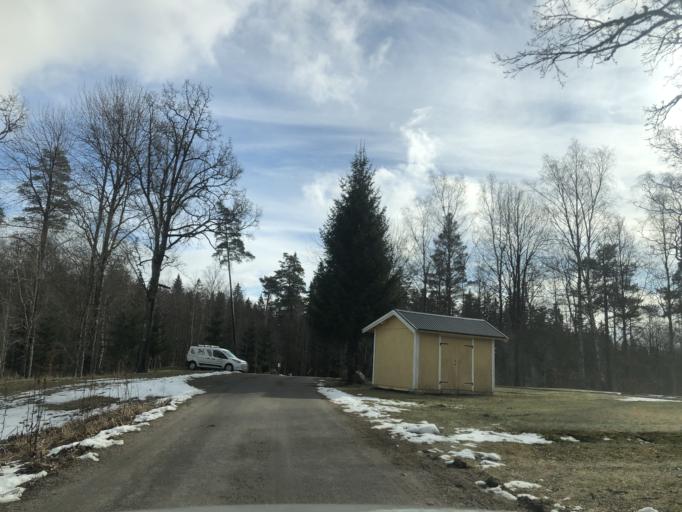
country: SE
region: Vaestra Goetaland
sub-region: Ulricehamns Kommun
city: Ulricehamn
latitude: 57.7831
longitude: 13.4391
